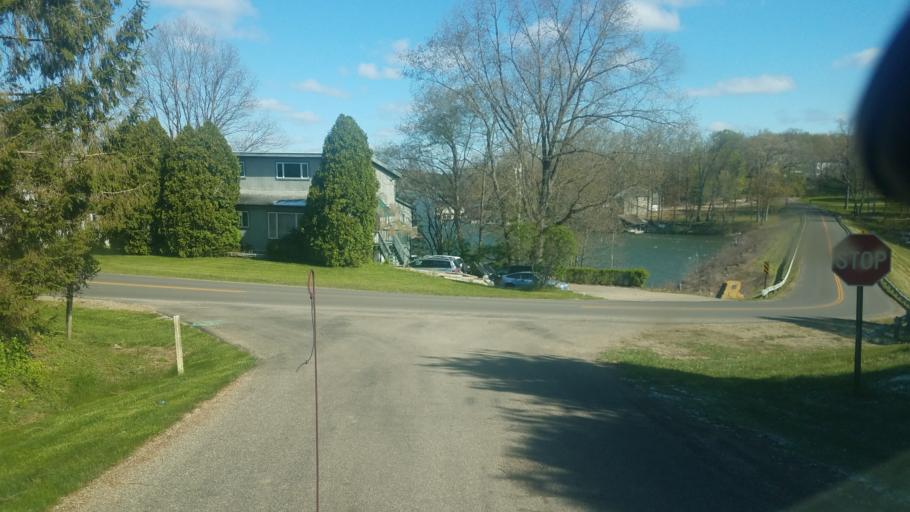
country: US
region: Ohio
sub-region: Knox County
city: Gambier
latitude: 40.4181
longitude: -82.3424
